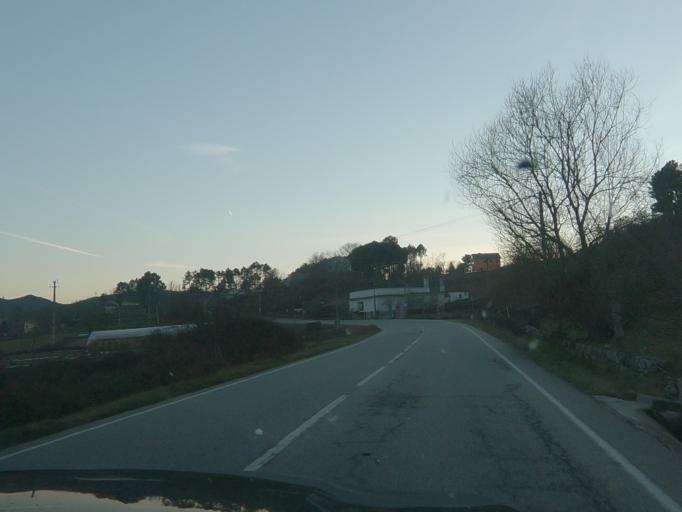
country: PT
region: Vila Real
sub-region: Vila Pouca de Aguiar
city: Vila Pouca de Aguiar
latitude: 41.4259
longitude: -7.6844
